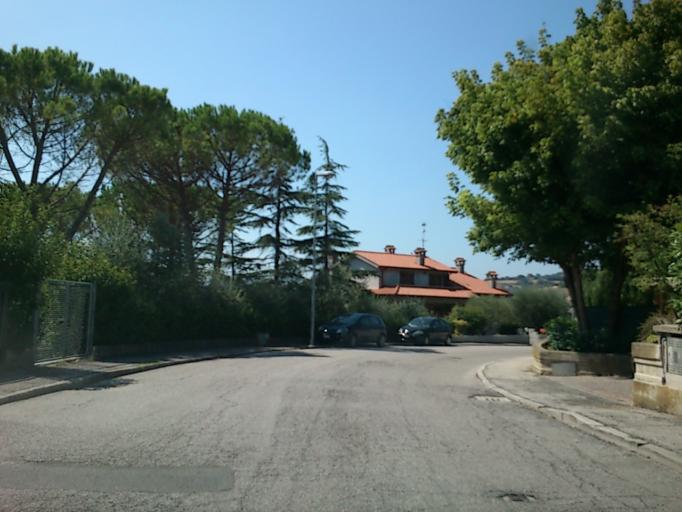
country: IT
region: The Marches
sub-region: Provincia di Pesaro e Urbino
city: Lucrezia
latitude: 43.7757
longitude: 12.9336
